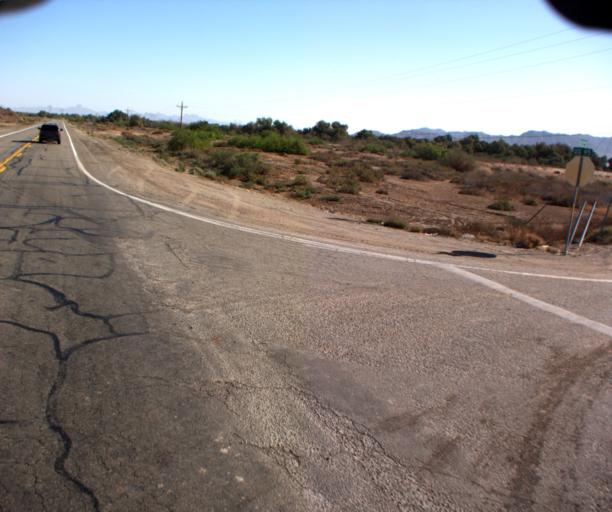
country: US
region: Arizona
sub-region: Yuma County
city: Fortuna Foothills
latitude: 32.7723
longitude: -114.3884
